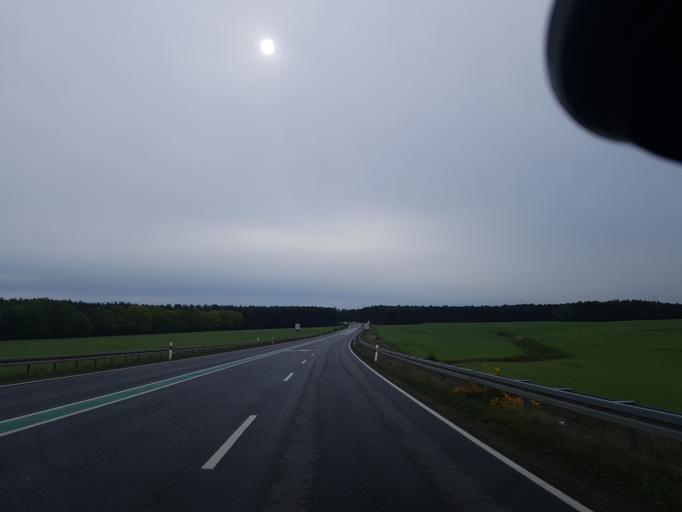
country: DE
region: Brandenburg
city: Drebkau
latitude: 51.6388
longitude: 14.2075
